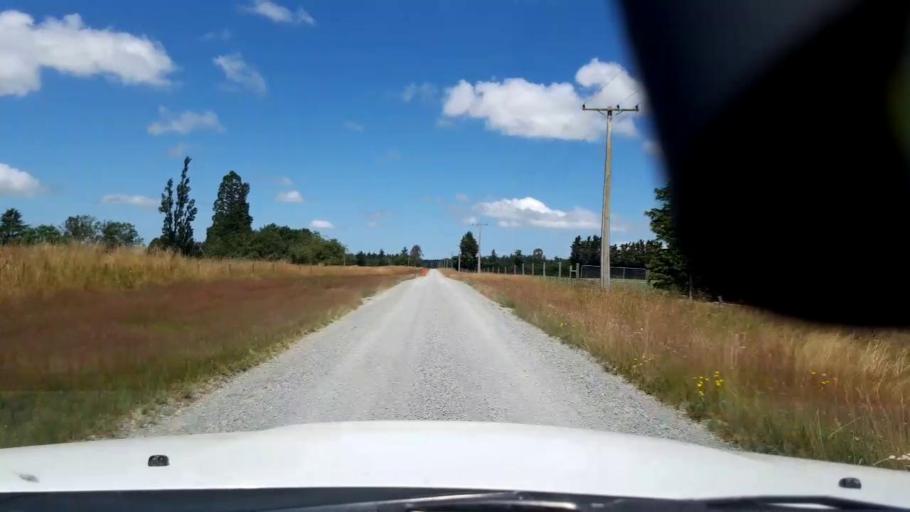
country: NZ
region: Canterbury
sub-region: Timaru District
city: Pleasant Point
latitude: -43.9831
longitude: 171.2876
